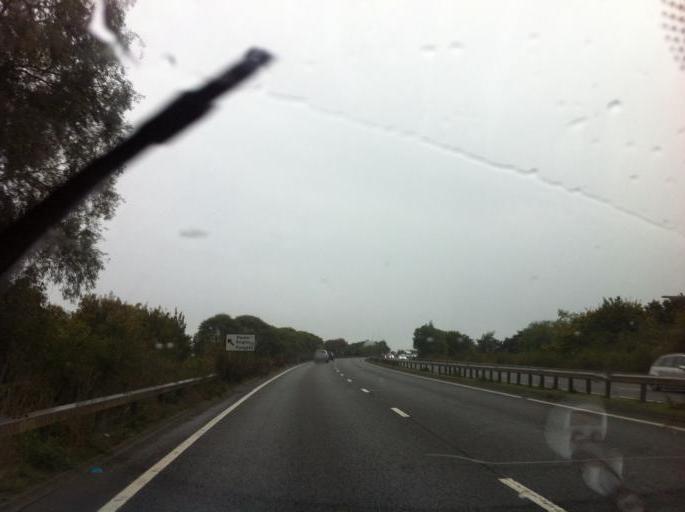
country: GB
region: England
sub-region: Peterborough
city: Peterborough
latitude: 52.5690
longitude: -0.2317
